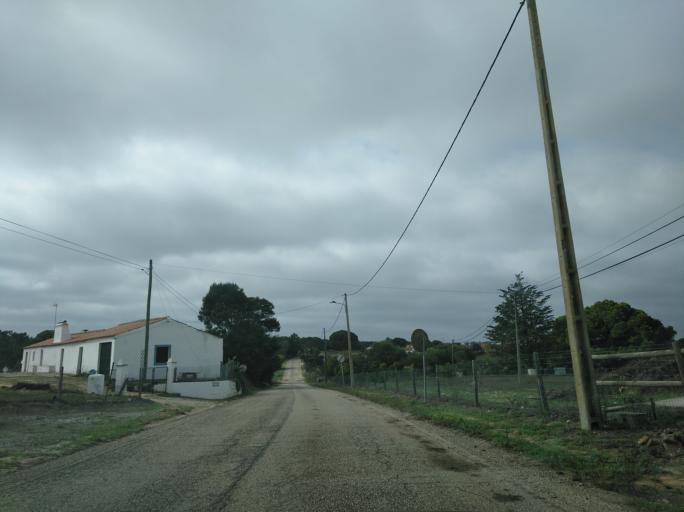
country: PT
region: Setubal
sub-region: Santiago do Cacem
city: Santo Andre
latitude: 38.1364
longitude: -8.7600
